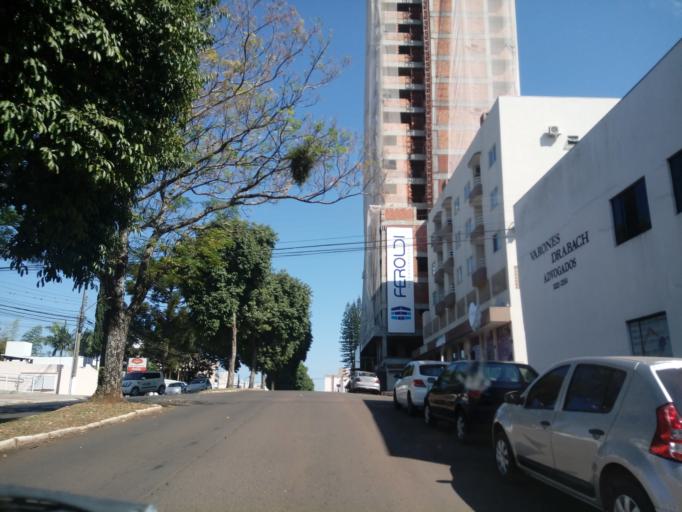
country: BR
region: Santa Catarina
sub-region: Chapeco
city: Chapeco
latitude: -27.0930
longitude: -52.6069
